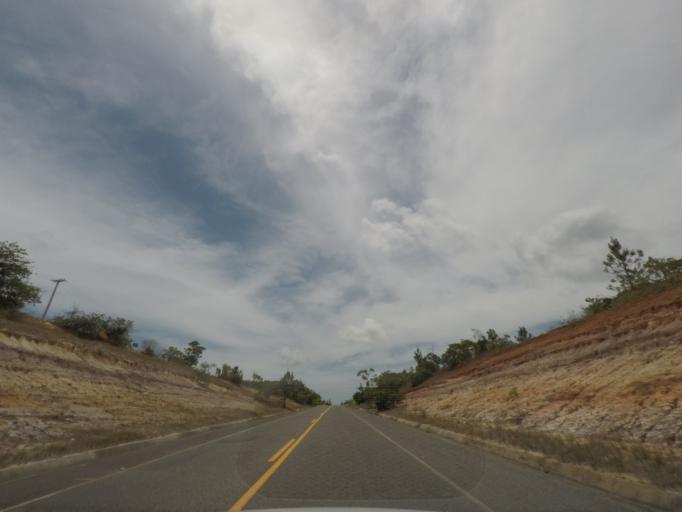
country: BR
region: Bahia
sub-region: Conde
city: Conde
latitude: -11.8983
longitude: -37.6522
